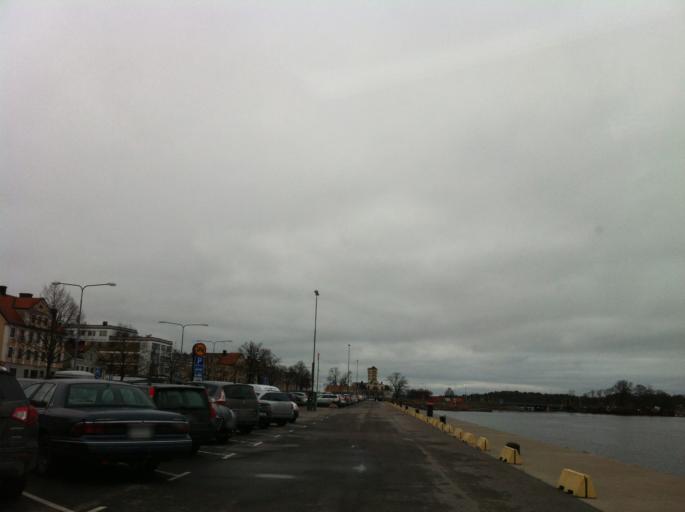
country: SE
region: Kalmar
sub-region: Vasterviks Kommun
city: Vaestervik
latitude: 57.7960
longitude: 16.6212
